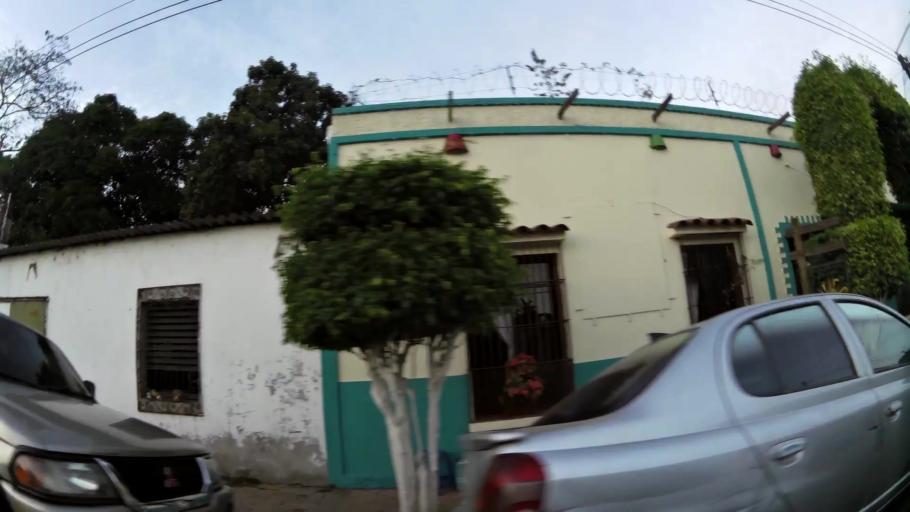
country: SV
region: Santa Ana
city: Santa Ana
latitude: 13.9904
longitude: -89.5610
